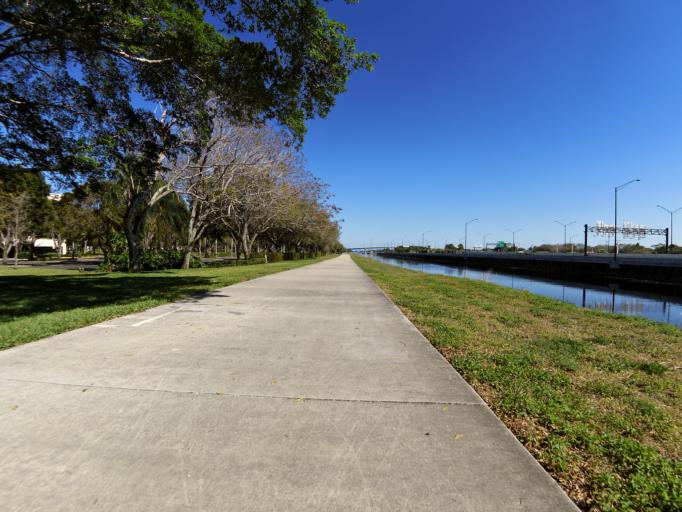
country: US
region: Florida
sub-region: Broward County
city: Pine Island Ridge
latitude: 26.1019
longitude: -80.2580
